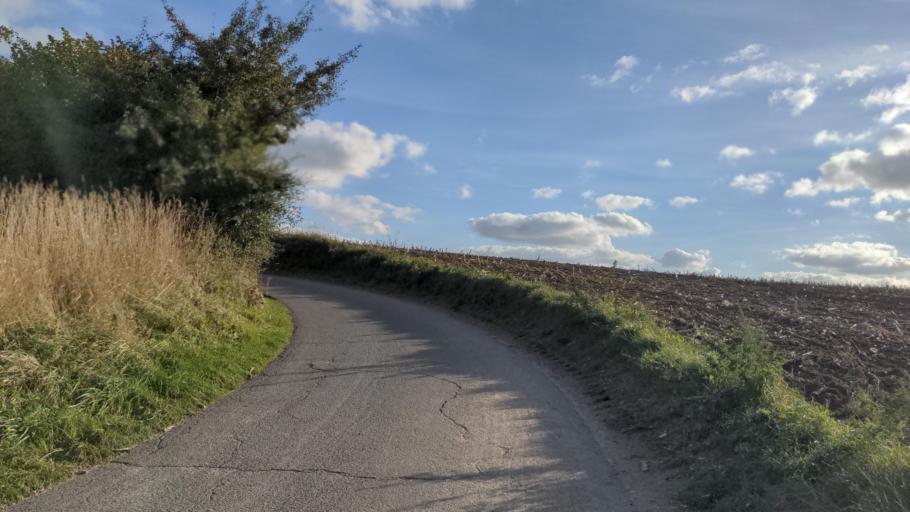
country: DE
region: Schleswig-Holstein
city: Schashagen
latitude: 54.1396
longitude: 10.9029
